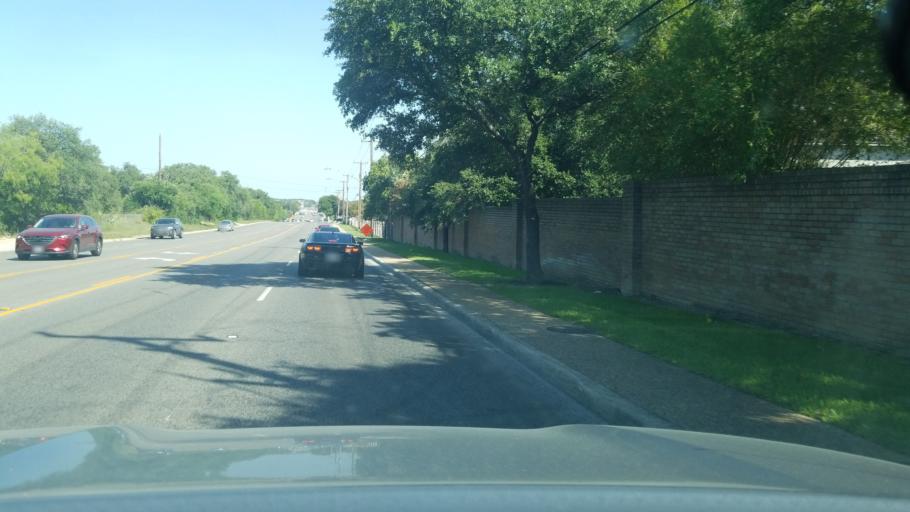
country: US
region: Texas
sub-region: Bexar County
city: Hollywood Park
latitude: 29.5707
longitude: -98.4900
